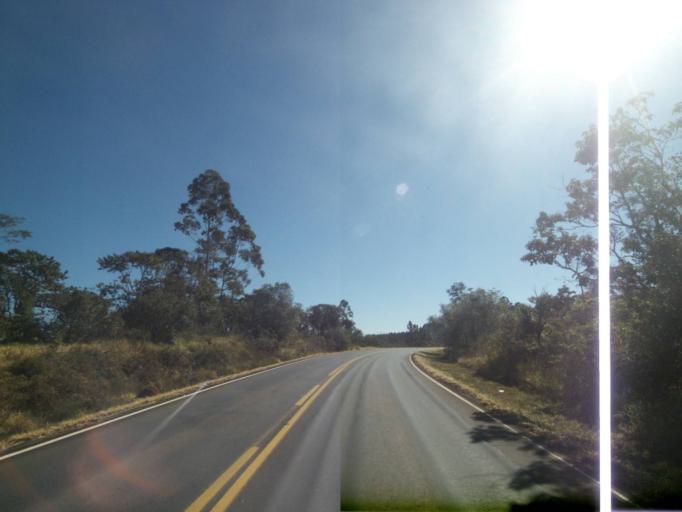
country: BR
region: Parana
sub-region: Tibagi
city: Tibagi
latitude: -24.4642
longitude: -50.5394
